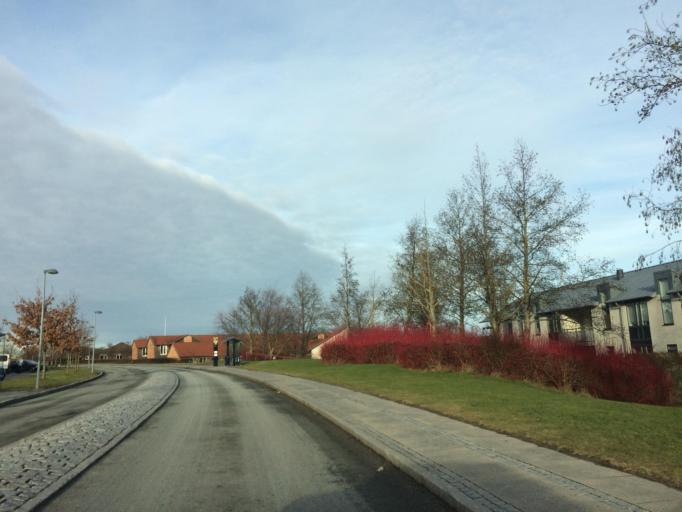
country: DK
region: Capital Region
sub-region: Fredensborg Kommune
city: Fredensborg
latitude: 55.9664
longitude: 12.4232
